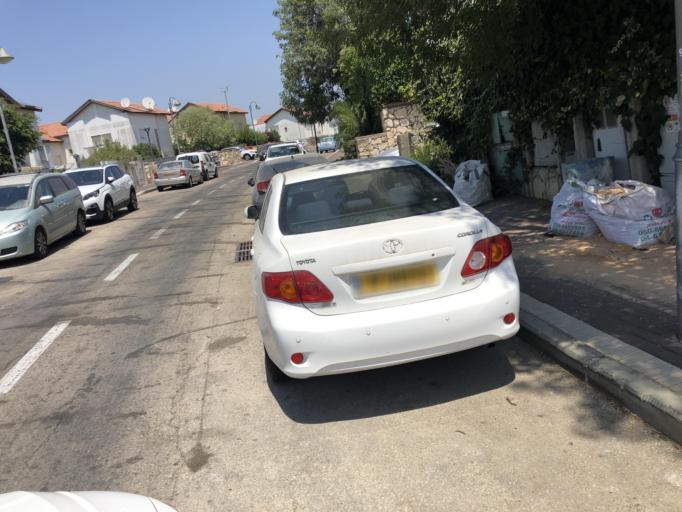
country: IL
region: Haifa
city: Daliyat el Karmil
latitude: 32.6384
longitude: 35.0862
